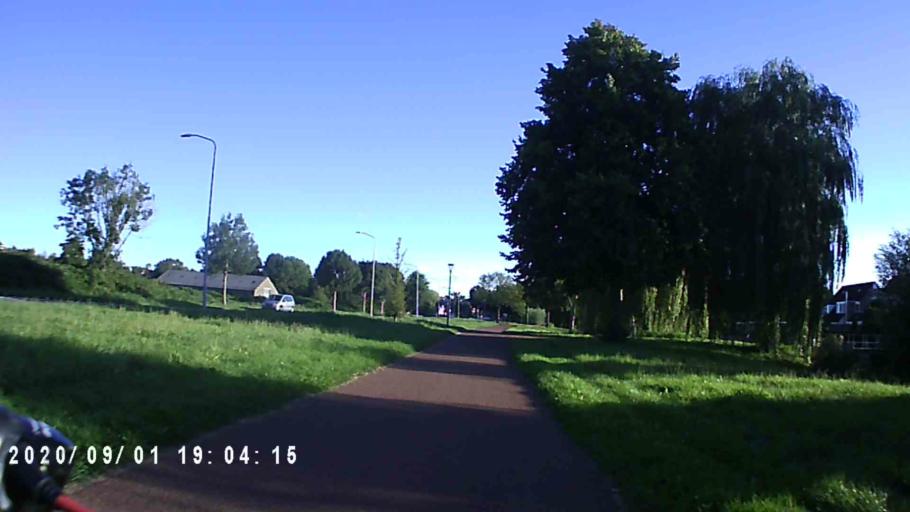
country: NL
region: Groningen
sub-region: Gemeente Veendam
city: Veendam
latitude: 53.1122
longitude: 6.8713
